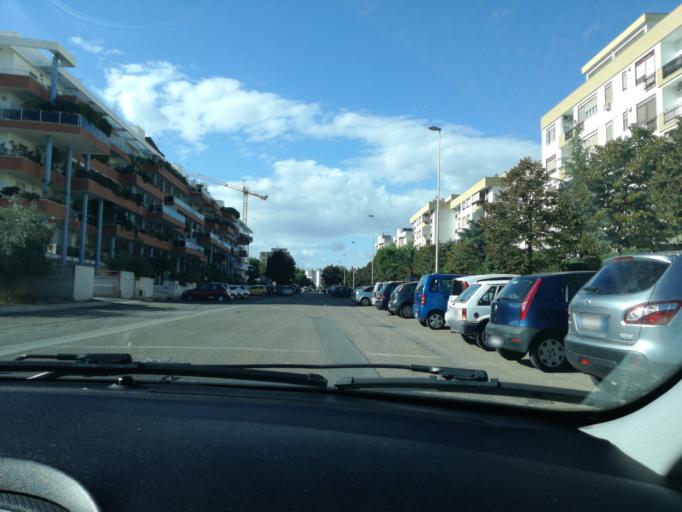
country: IT
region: Apulia
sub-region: Provincia di Bari
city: Triggiano
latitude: 41.0731
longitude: 16.9324
